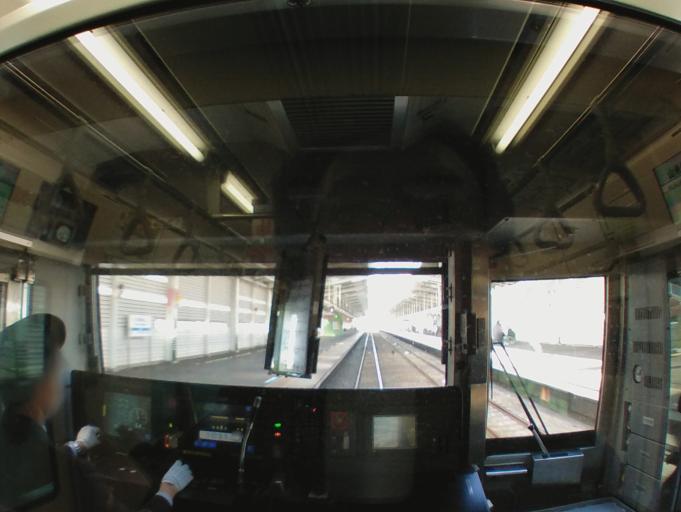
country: JP
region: Tokyo
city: Hino
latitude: 35.6286
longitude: 139.4521
